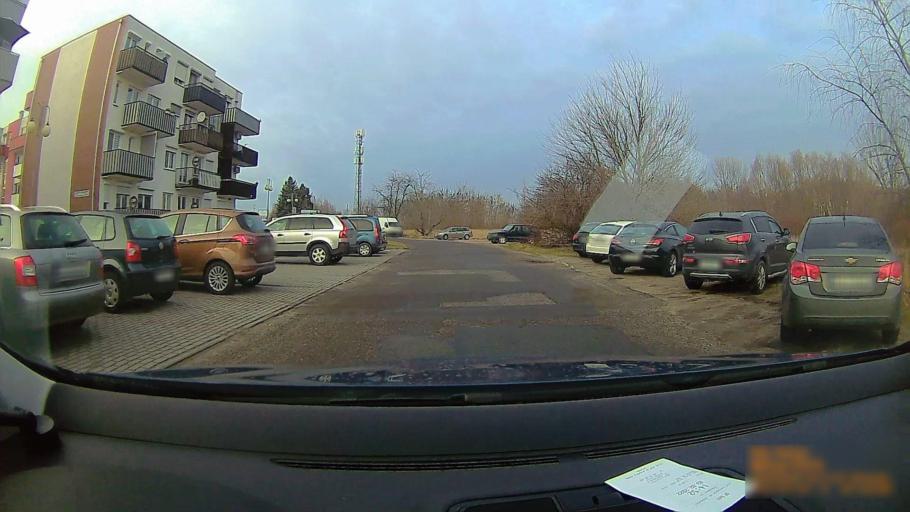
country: PL
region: Greater Poland Voivodeship
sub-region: Konin
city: Konin
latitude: 52.2354
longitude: 18.2182
